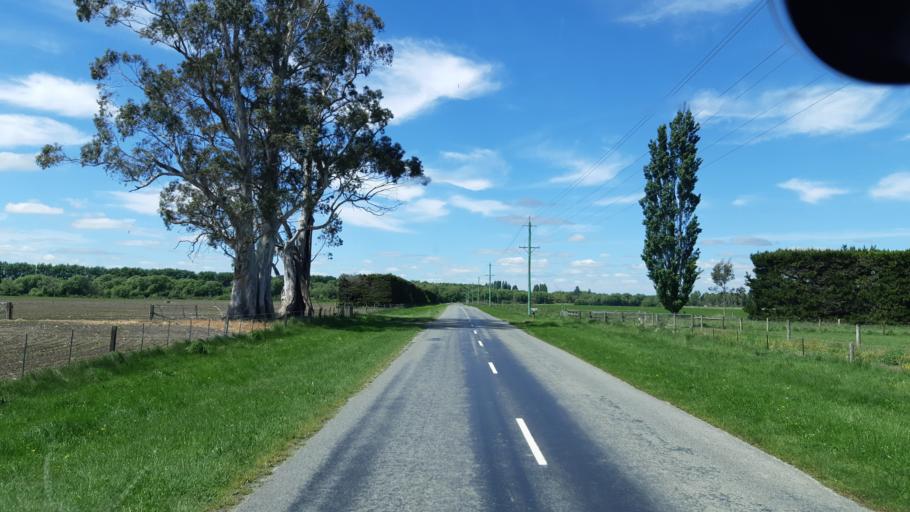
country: NZ
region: Canterbury
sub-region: Ashburton District
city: Methven
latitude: -43.7316
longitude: 171.5208
